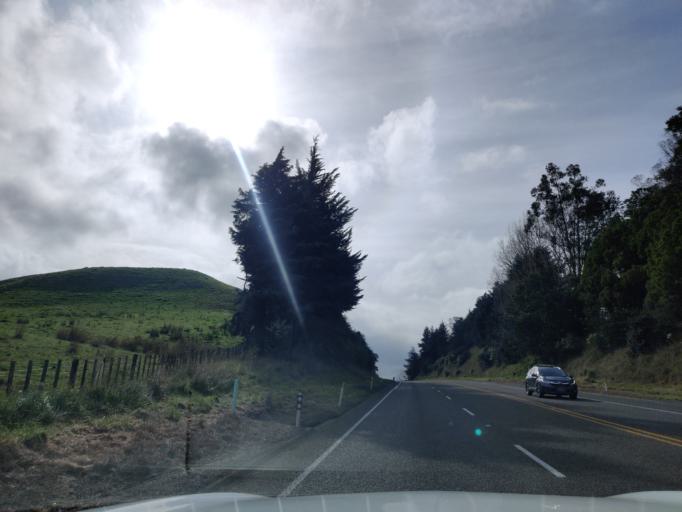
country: NZ
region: Manawatu-Wanganui
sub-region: Ruapehu District
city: Waiouru
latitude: -39.7713
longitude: 175.7962
